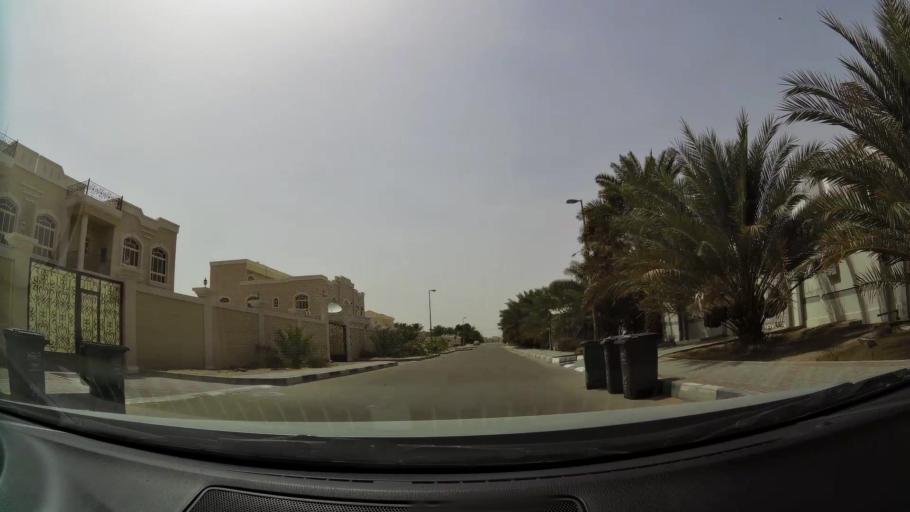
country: AE
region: Abu Dhabi
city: Al Ain
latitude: 24.1528
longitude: 55.6549
